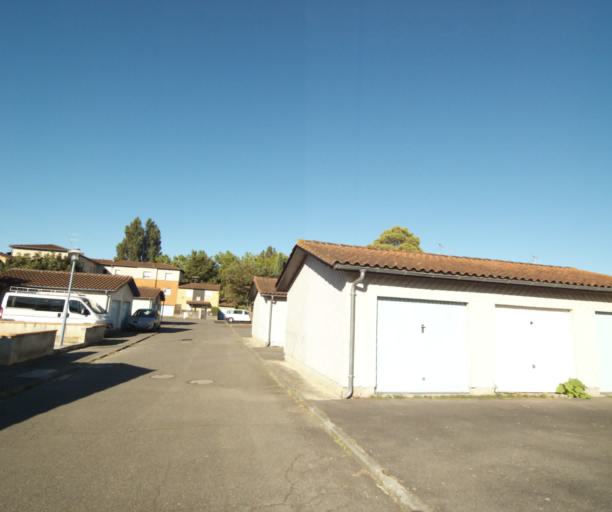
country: FR
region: Midi-Pyrenees
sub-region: Departement de la Haute-Garonne
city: Castanet-Tolosan
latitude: 43.5215
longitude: 1.5062
